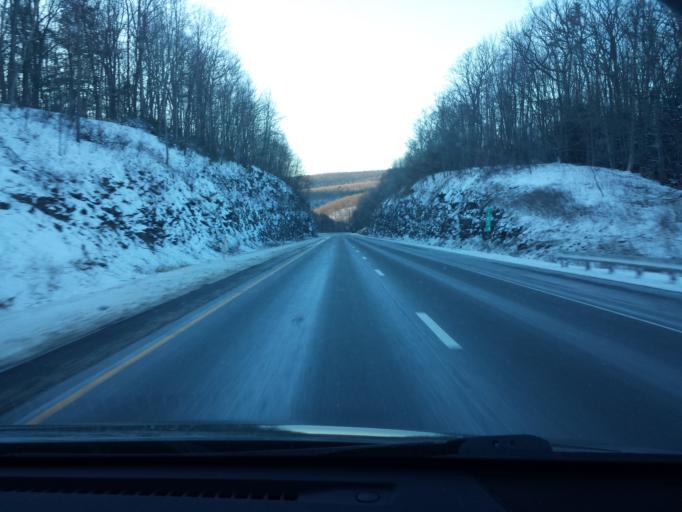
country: US
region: Pennsylvania
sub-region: Clinton County
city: Castanea
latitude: 41.0592
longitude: -77.3608
